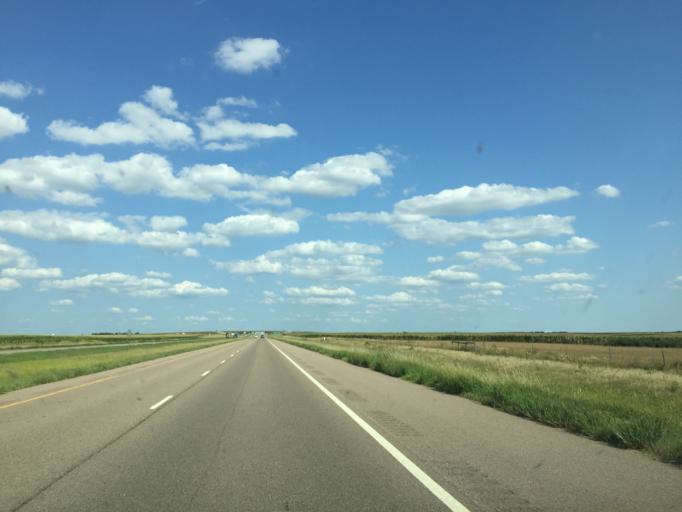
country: US
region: Kansas
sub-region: Gove County
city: Gove
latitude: 39.1050
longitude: -100.4568
